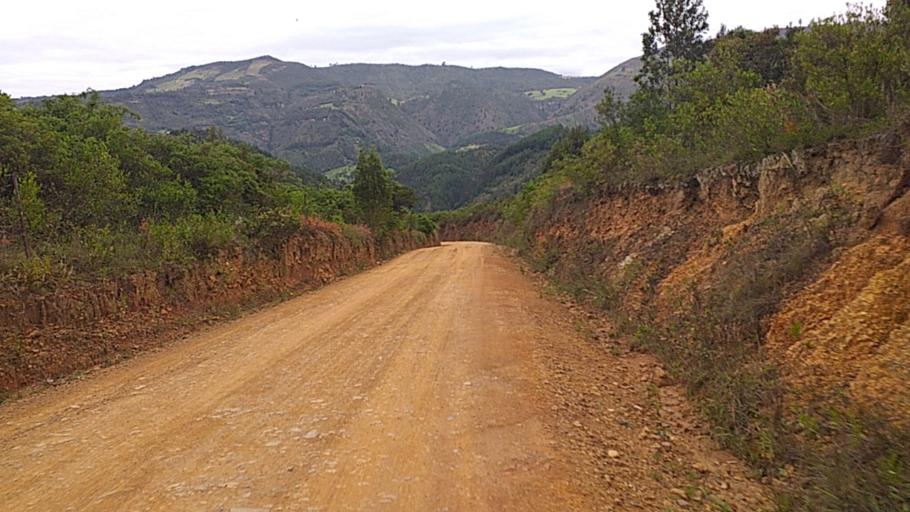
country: CO
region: Boyaca
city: Floresta
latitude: 5.8797
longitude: -72.9123
